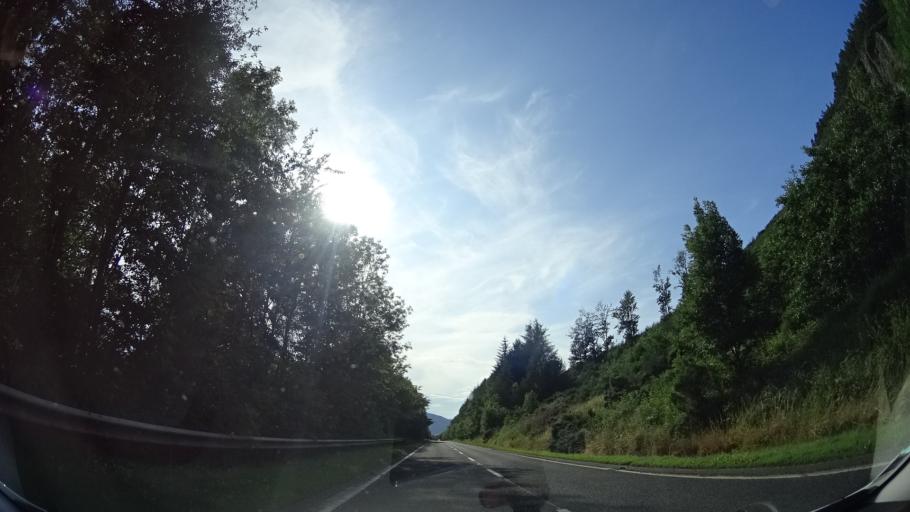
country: GB
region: Scotland
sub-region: Highland
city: Muir of Ord
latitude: 57.5583
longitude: -4.5178
